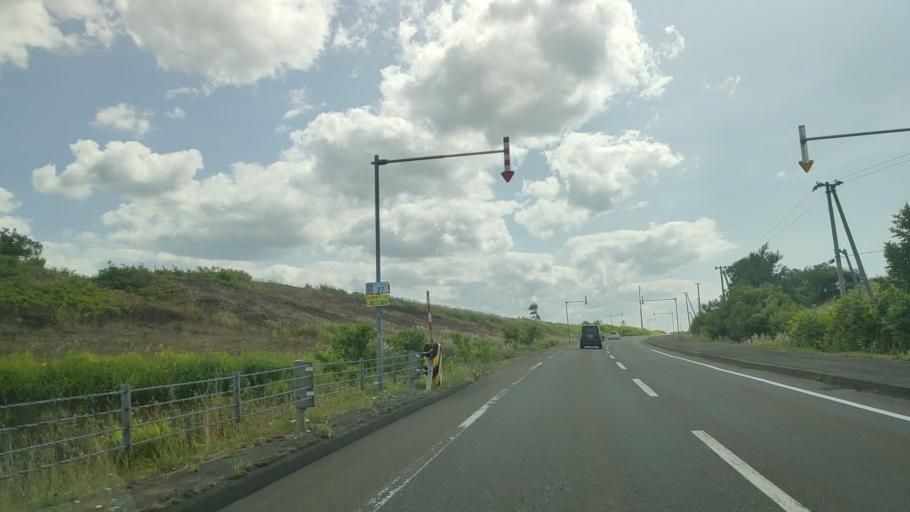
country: JP
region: Hokkaido
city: Makubetsu
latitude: 44.7917
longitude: 141.7902
